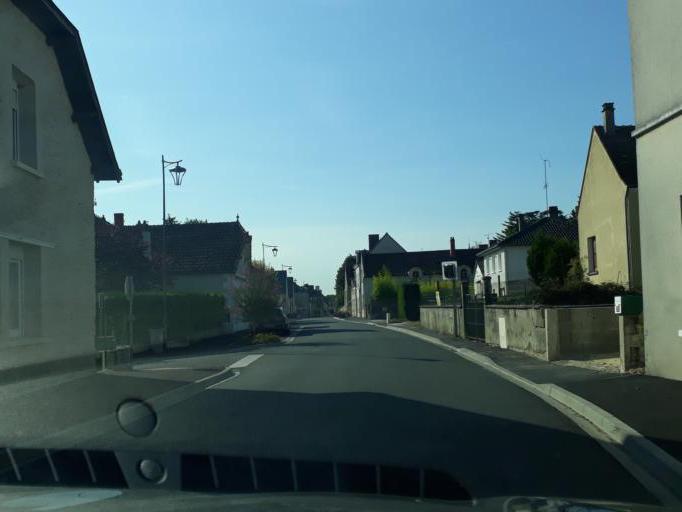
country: FR
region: Centre
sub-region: Departement du Loir-et-Cher
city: Thesee
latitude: 47.3249
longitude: 1.3076
